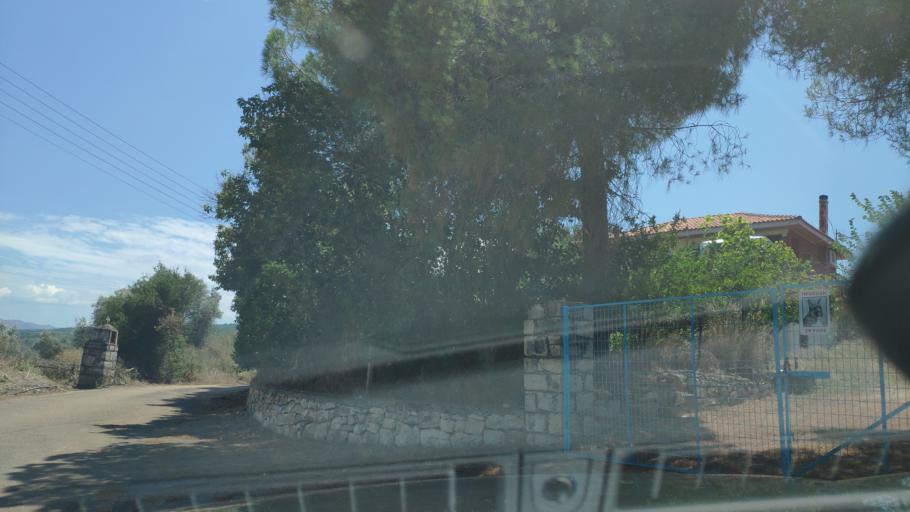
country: GR
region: West Greece
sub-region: Nomos Aitolias kai Akarnanias
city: Amfilochia
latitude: 38.9096
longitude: 21.1061
